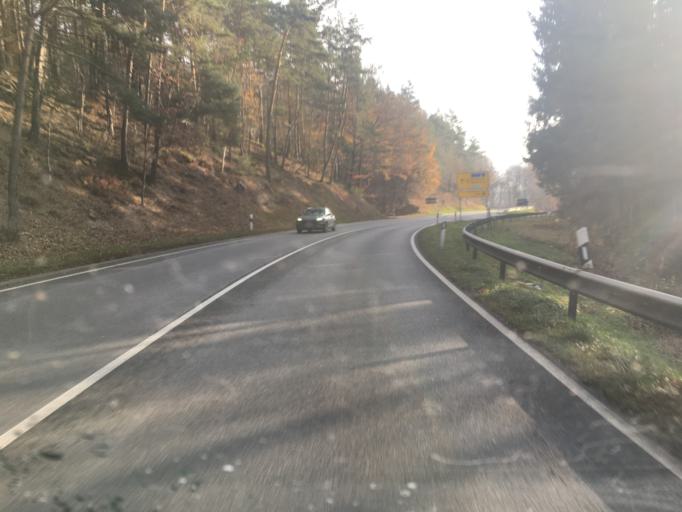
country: DE
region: North Rhine-Westphalia
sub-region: Regierungsbezirk Koln
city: Kall
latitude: 50.5573
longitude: 6.5413
